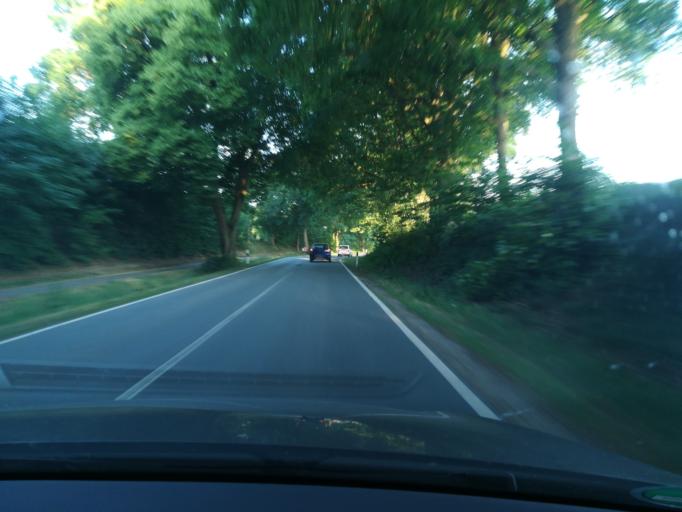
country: DE
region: Schleswig-Holstein
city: Grossensee
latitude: 53.6105
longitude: 10.3542
